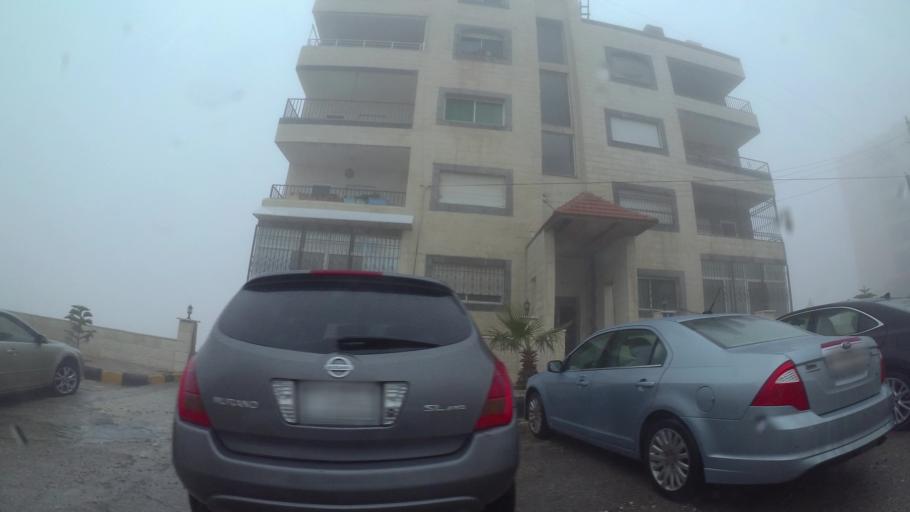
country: JO
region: Amman
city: Al Jubayhah
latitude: 32.0041
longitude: 35.8904
